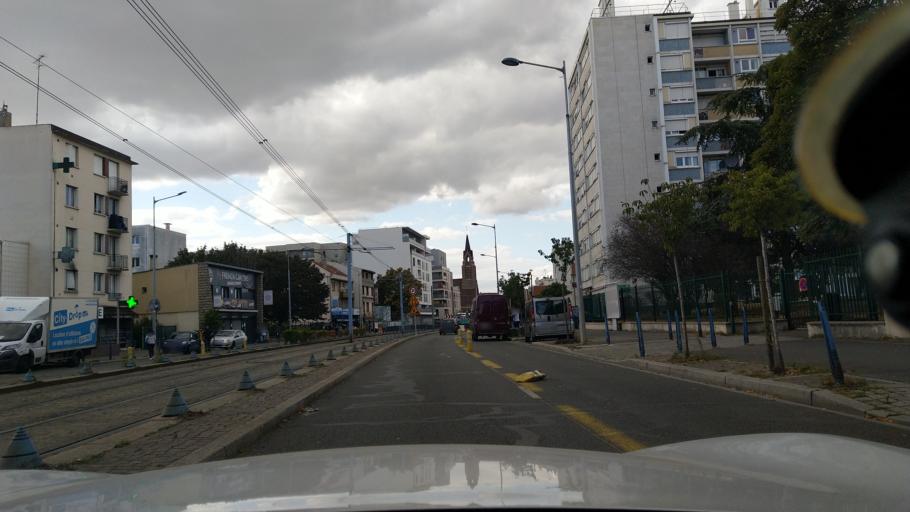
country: FR
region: Ile-de-France
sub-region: Departement de Seine-Saint-Denis
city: La Courneuve
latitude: 48.9185
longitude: 2.4158
